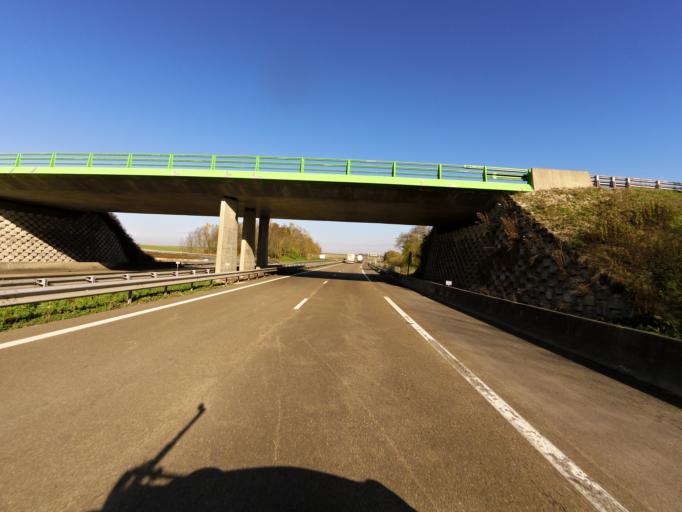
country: FR
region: Champagne-Ardenne
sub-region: Departement de la Marne
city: Fagnieres
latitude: 48.9699
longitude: 4.2840
